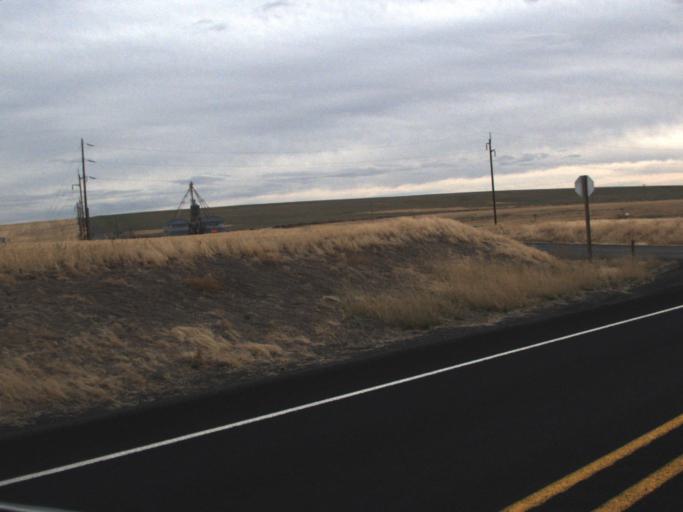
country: US
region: Washington
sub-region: Okanogan County
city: Coulee Dam
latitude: 47.7726
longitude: -118.7240
